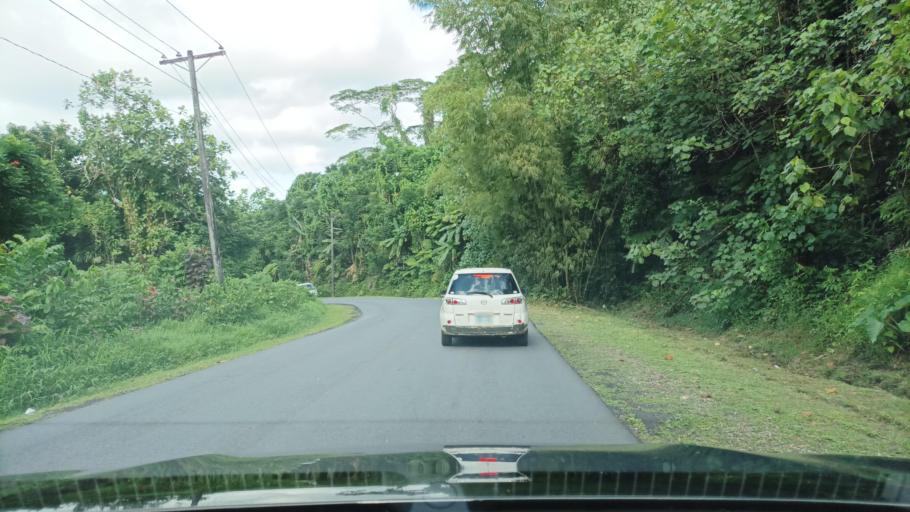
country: FM
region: Pohnpei
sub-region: Sokehs Municipality
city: Palikir - National Government Center
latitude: 6.9263
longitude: 158.1753
